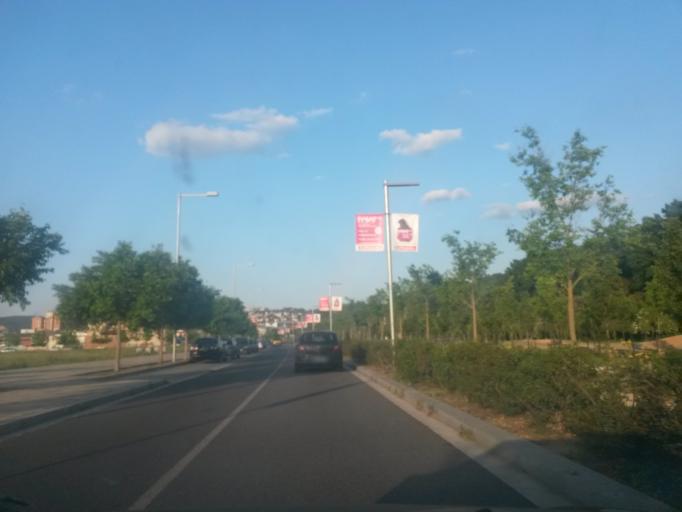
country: ES
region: Catalonia
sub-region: Provincia de Girona
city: Salt
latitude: 41.9895
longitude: 2.8047
